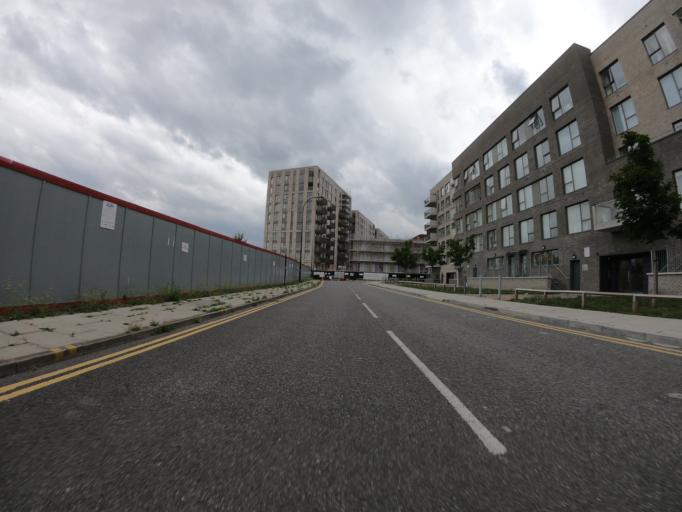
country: GB
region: England
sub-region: Greater London
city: Woolwich
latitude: 51.5077
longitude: 0.0784
